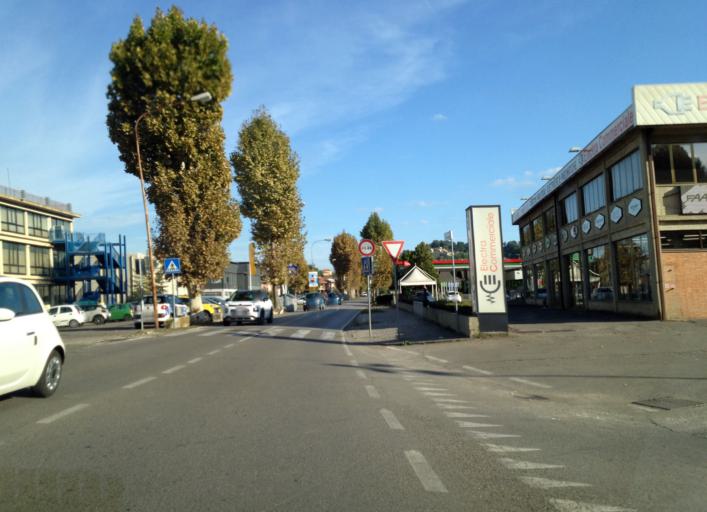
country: IT
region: Tuscany
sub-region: Provincia di Siena
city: Poggibonsi
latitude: 43.4693
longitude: 11.1345
